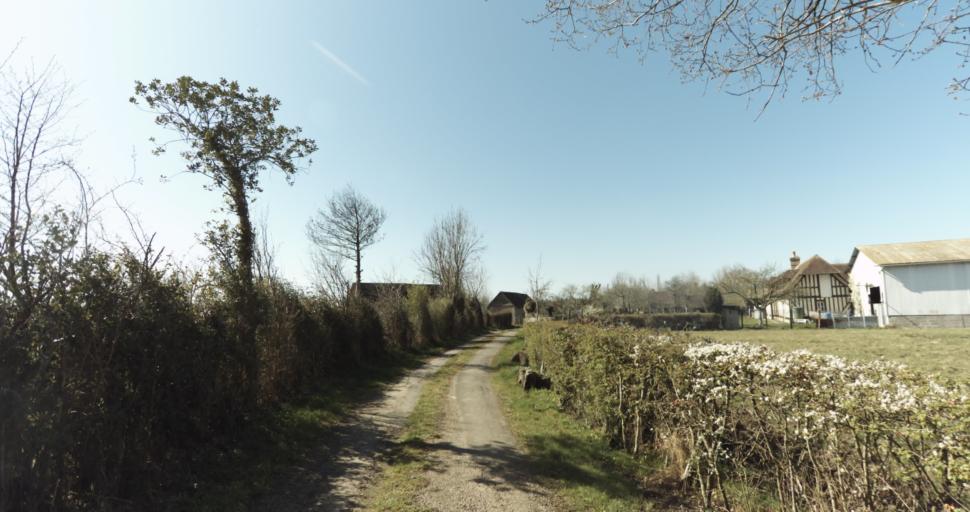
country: FR
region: Lower Normandy
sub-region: Departement du Calvados
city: Livarot
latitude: 49.0232
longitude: 0.1032
